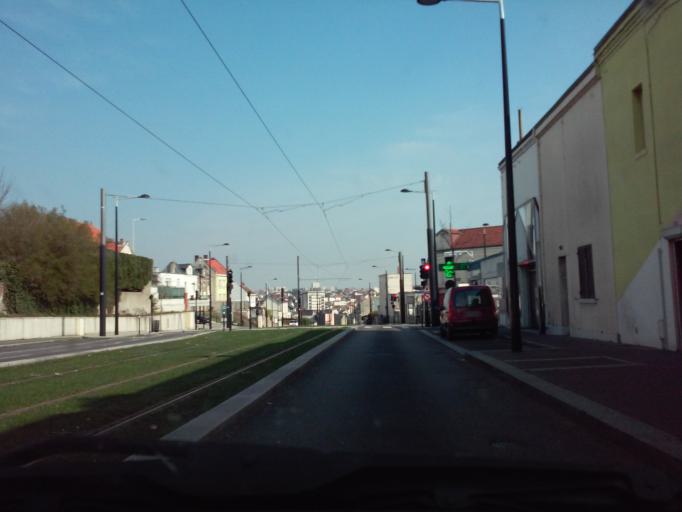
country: FR
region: Haute-Normandie
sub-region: Departement de la Seine-Maritime
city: Le Havre
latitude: 49.5106
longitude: 0.1301
